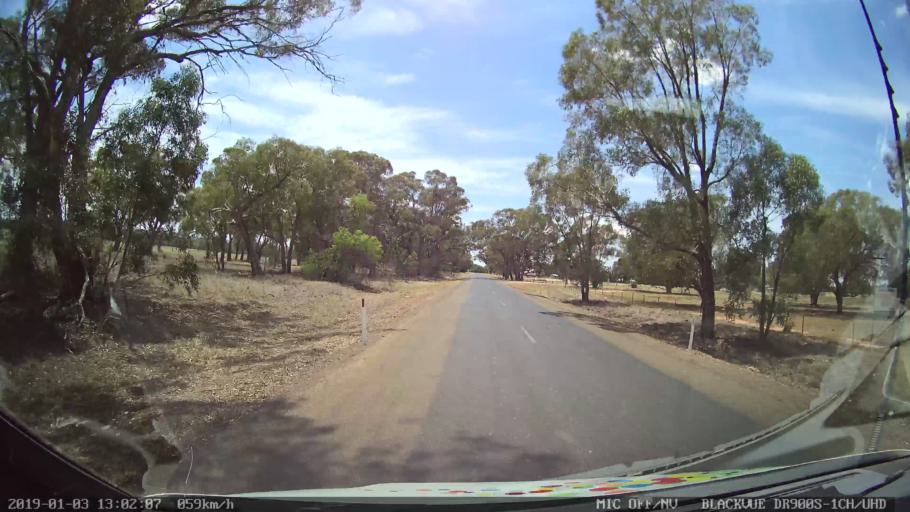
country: AU
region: New South Wales
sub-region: Cabonne
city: Canowindra
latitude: -33.6196
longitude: 148.4262
